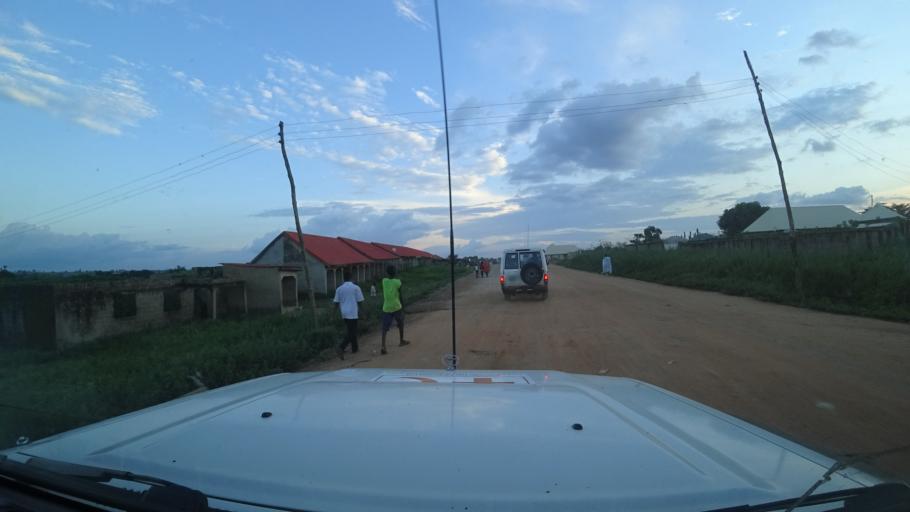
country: NG
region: Niger
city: Minna
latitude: 9.6418
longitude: 6.5803
